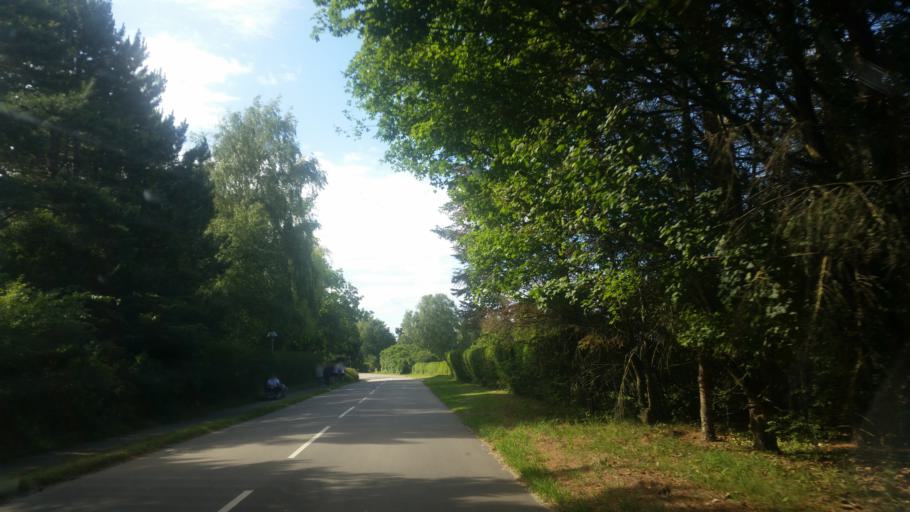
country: DK
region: Zealand
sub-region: Odsherred Kommune
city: Horve
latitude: 55.8254
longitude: 11.3999
